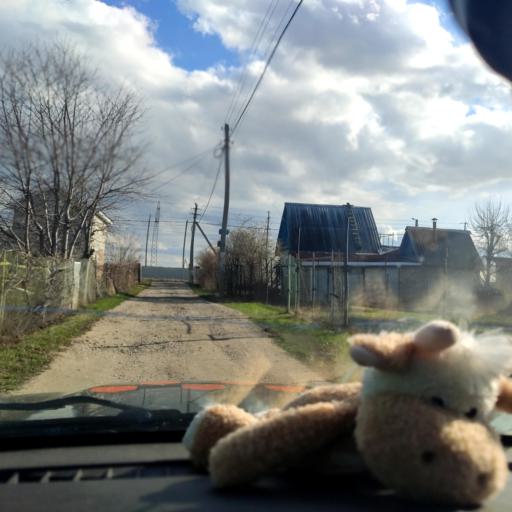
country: RU
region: Samara
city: Tol'yatti
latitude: 53.5915
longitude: 49.3080
